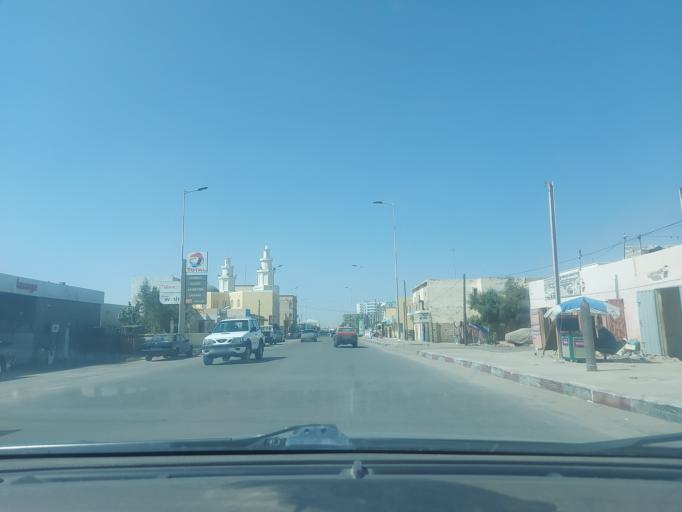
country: MR
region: Nouakchott
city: Nouakchott
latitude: 18.1006
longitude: -15.9574
